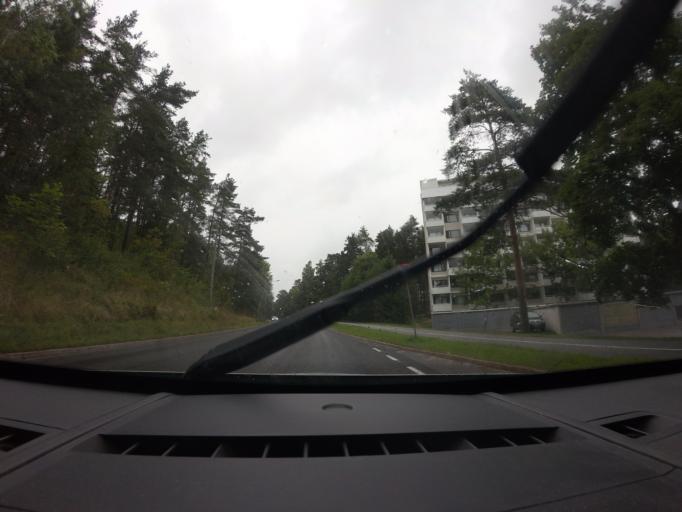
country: FI
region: Varsinais-Suomi
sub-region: Turku
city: Turku
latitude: 60.4302
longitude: 22.2886
